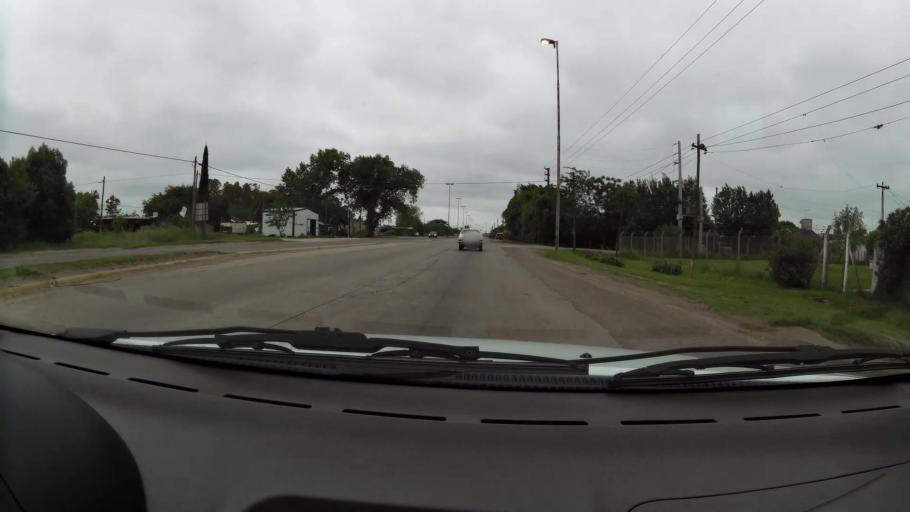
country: AR
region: Buenos Aires
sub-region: Partido de La Plata
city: La Plata
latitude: -35.0253
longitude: -58.0811
